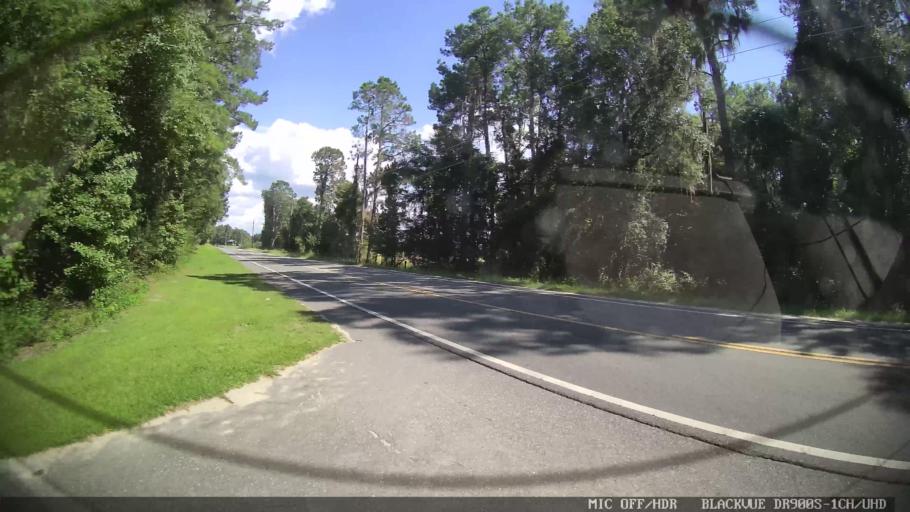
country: US
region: Georgia
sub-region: Echols County
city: Statenville
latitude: 30.5740
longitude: -83.1649
